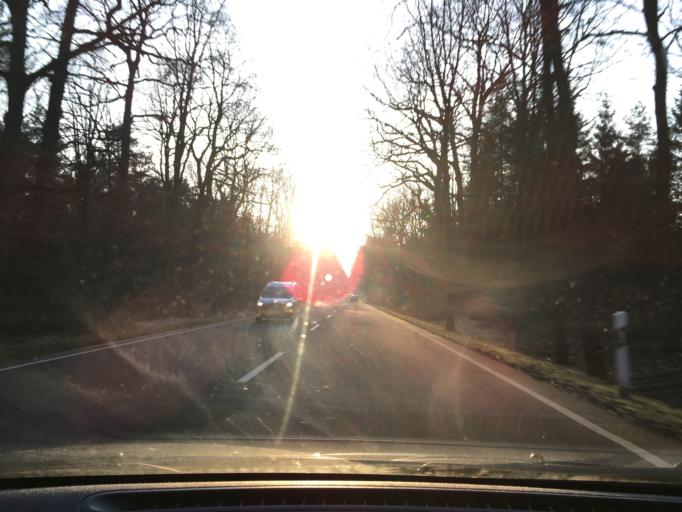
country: DE
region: Lower Saxony
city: Sprakensehl
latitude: 52.8155
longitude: 10.4405
